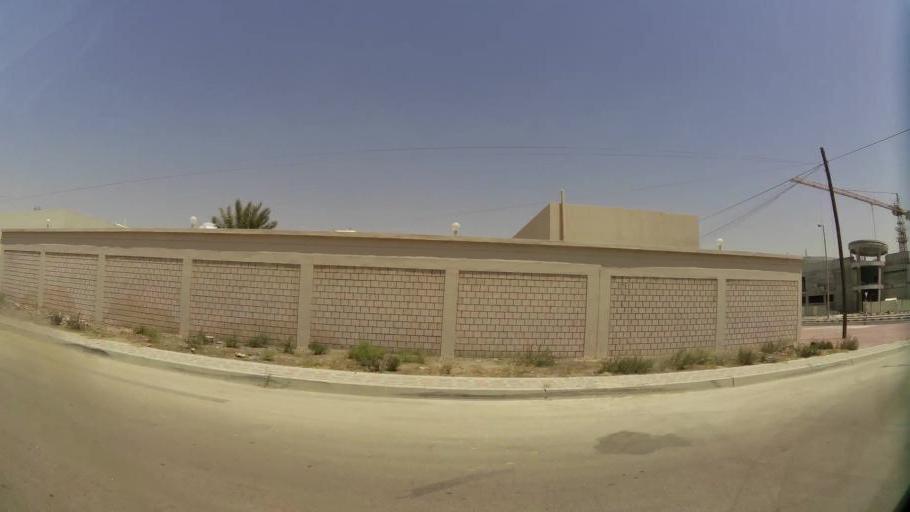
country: AE
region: Ajman
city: Ajman
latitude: 25.4185
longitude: 55.5044
